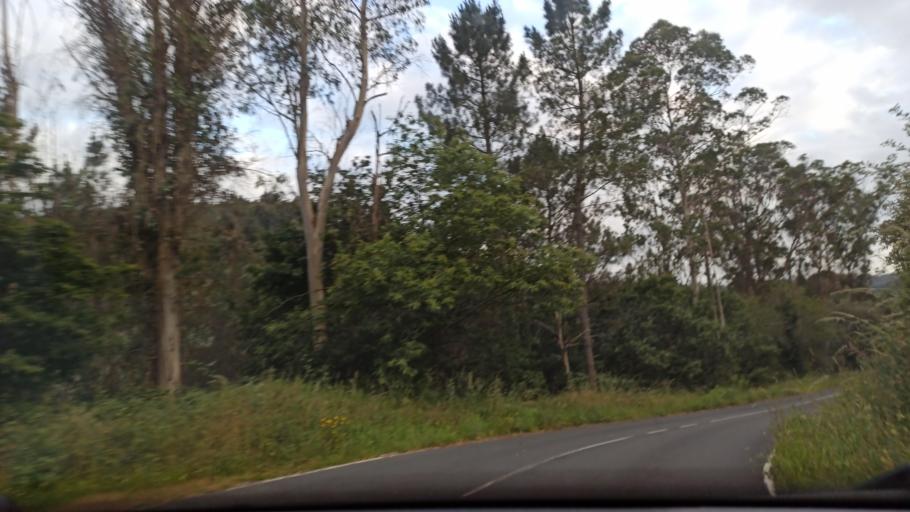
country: ES
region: Galicia
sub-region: Provincia da Coruna
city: Santiso
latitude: 42.8166
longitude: -8.1393
